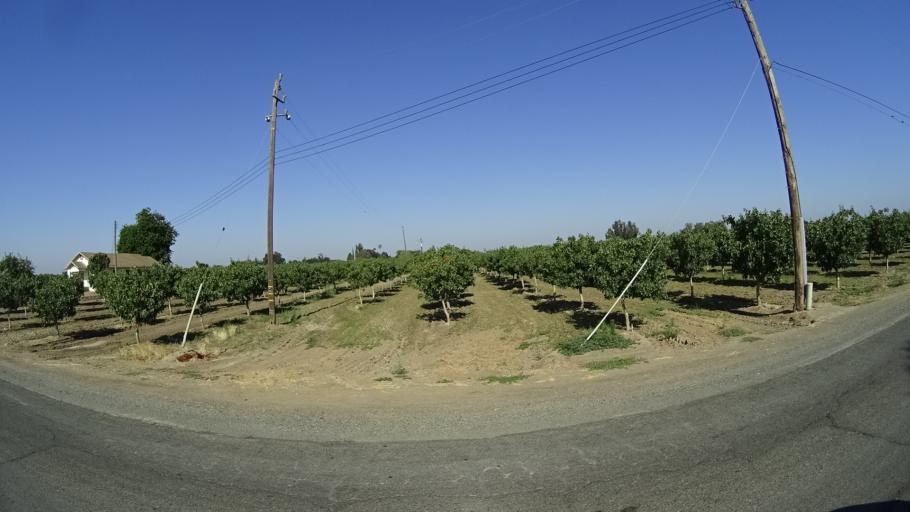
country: US
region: California
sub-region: Kings County
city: Lucerne
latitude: 36.3889
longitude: -119.6910
